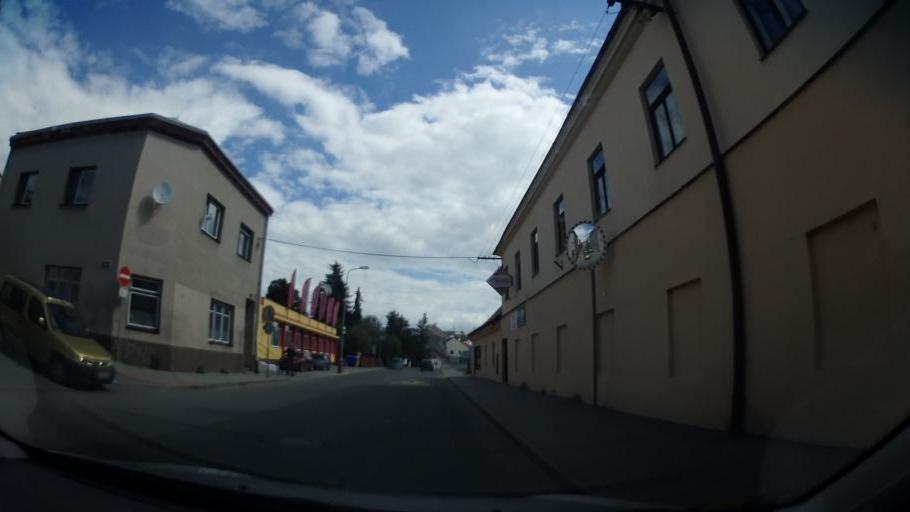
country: CZ
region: Pardubicky
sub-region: Okres Svitavy
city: Moravska Trebova
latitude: 49.7540
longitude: 16.6585
